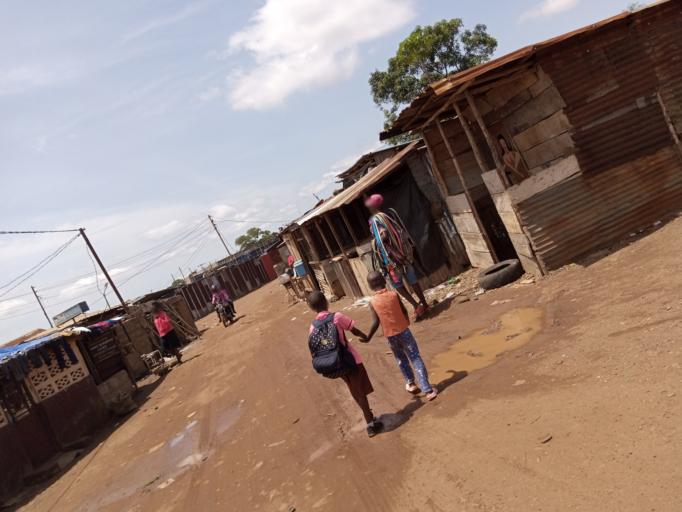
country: SL
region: Western Area
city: Hastings
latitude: 8.3858
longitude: -13.1362
